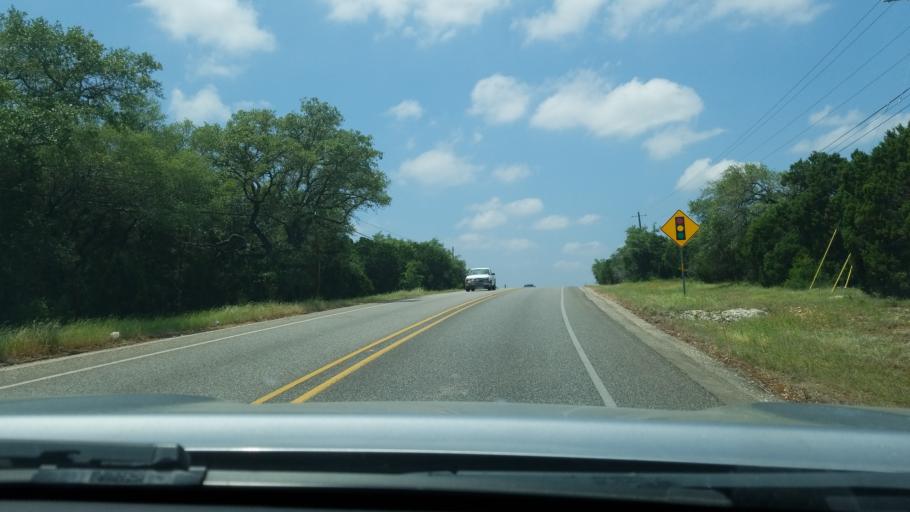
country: US
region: Texas
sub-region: Hays County
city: Woodcreek
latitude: 30.0167
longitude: -98.1266
